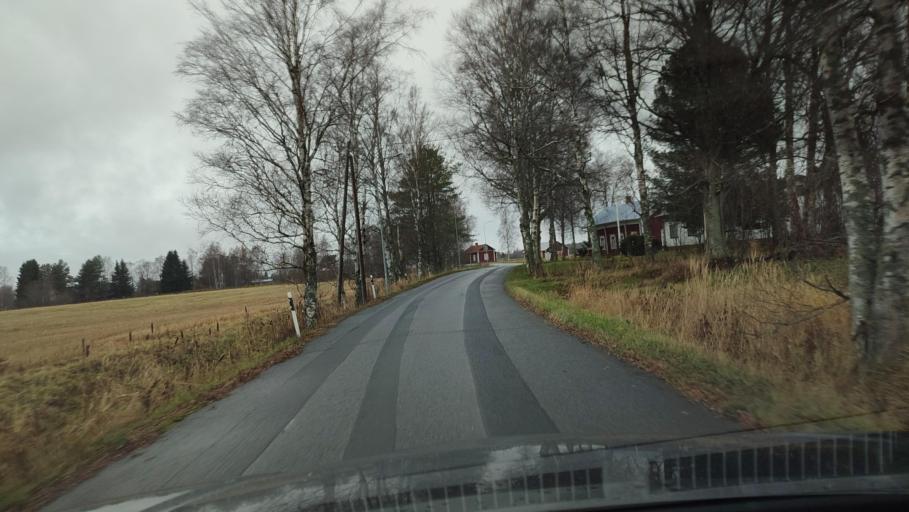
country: FI
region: Ostrobothnia
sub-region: Sydosterbotten
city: Kristinestad
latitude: 62.2522
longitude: 21.5429
